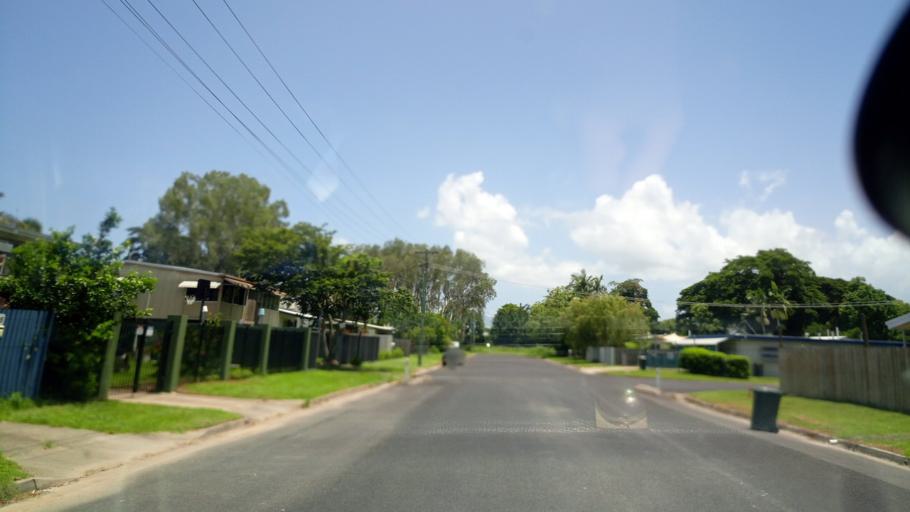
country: AU
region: Queensland
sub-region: Cairns
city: Woree
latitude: -16.9402
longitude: 145.7469
